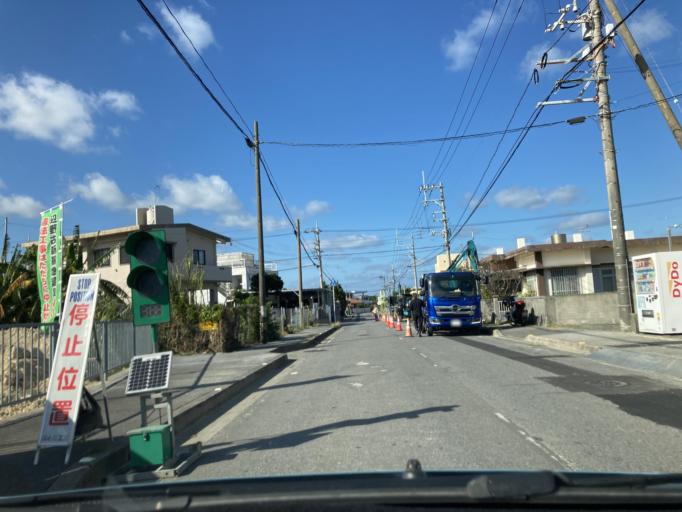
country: JP
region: Okinawa
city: Katsuren-haebaru
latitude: 26.3151
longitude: 127.9095
